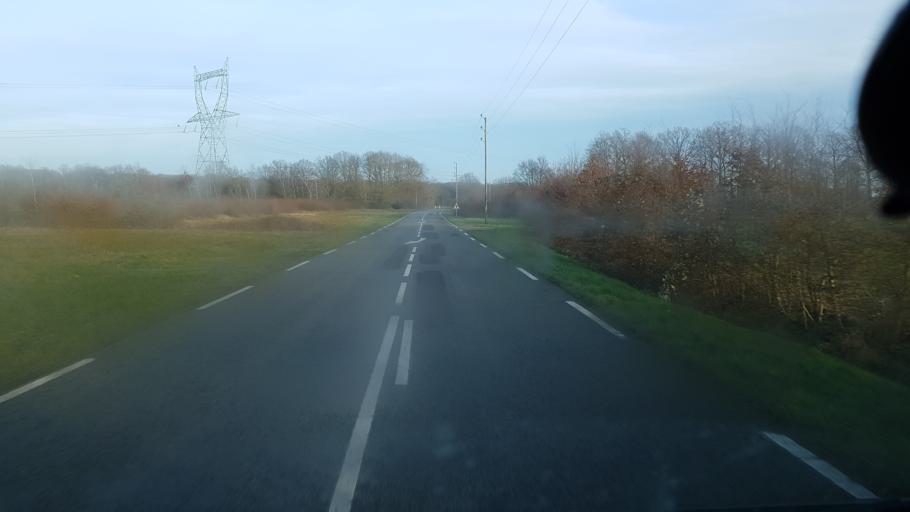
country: FR
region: Ile-de-France
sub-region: Departement des Yvelines
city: Auffargis
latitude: 48.6824
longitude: 1.8828
